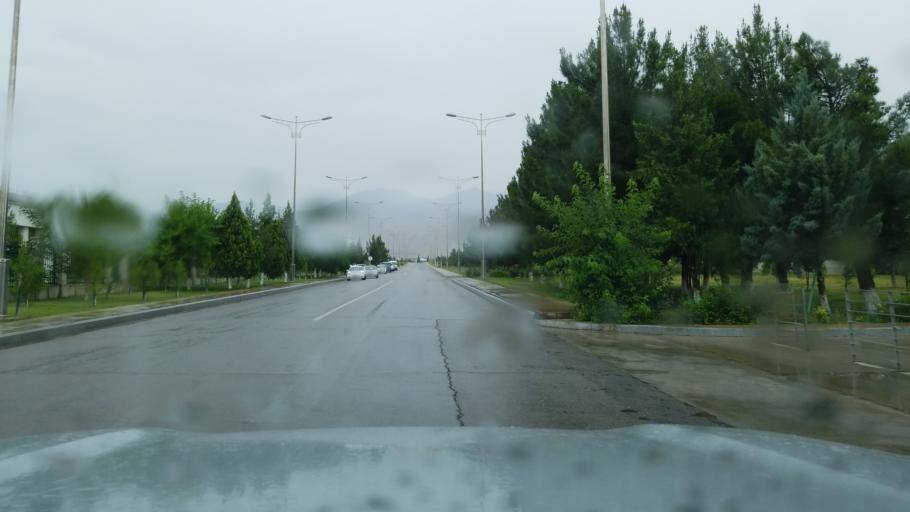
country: TM
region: Ahal
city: Ashgabat
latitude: 37.8911
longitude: 58.3431
